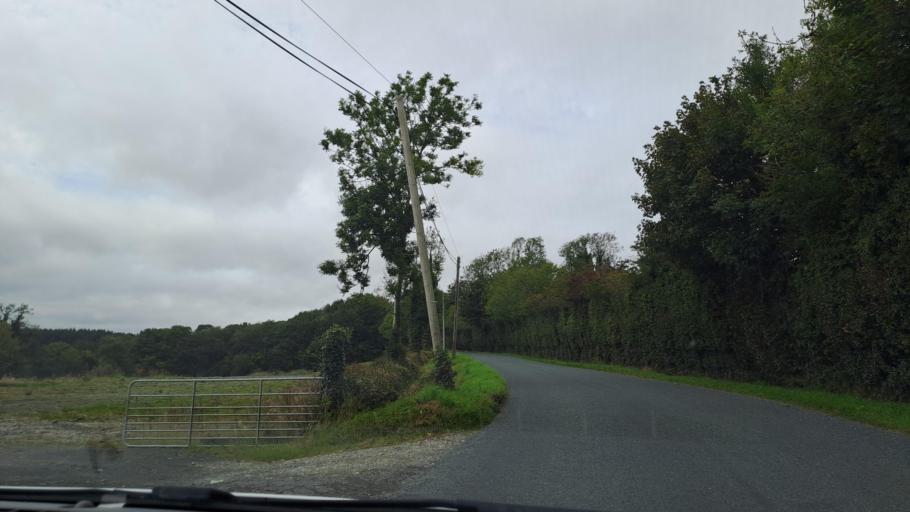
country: IE
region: Ulster
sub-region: An Cabhan
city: Bailieborough
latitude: 53.9965
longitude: -6.9053
